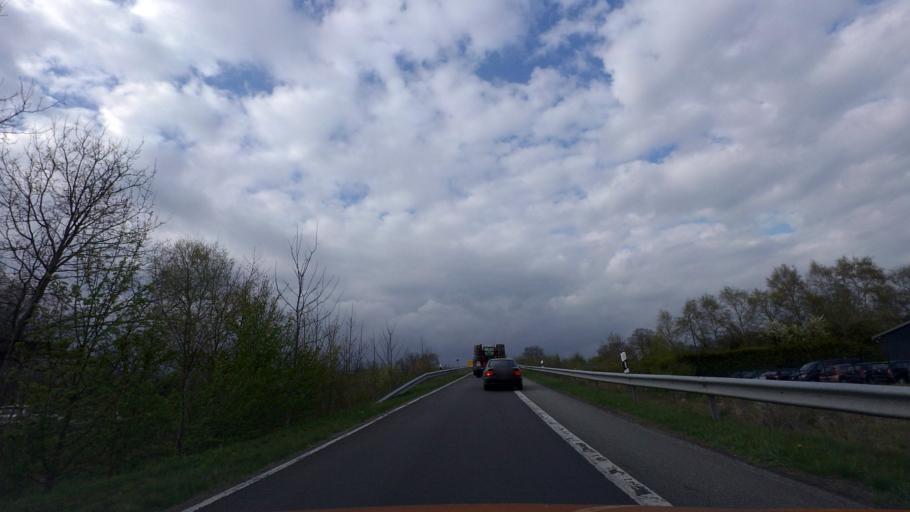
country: DE
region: Lower Saxony
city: Friesoythe
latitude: 53.0073
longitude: 7.8644
